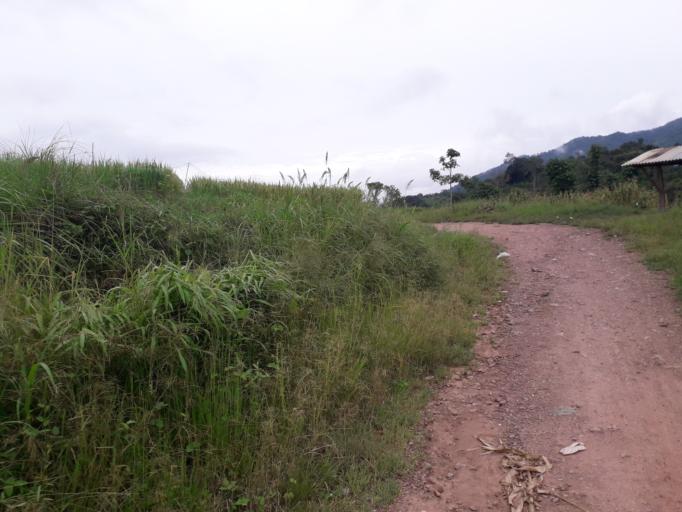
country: CN
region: Yunnan
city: Menglie
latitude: 22.2492
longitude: 101.6060
